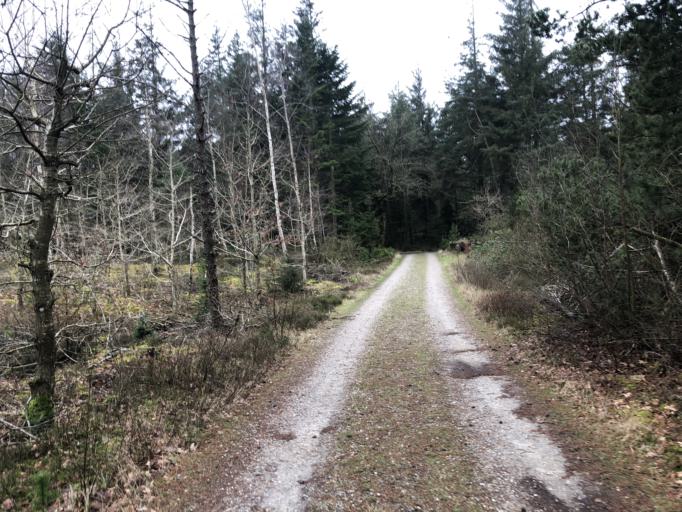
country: DK
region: Central Jutland
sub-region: Holstebro Kommune
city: Ulfborg
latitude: 56.2895
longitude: 8.1722
